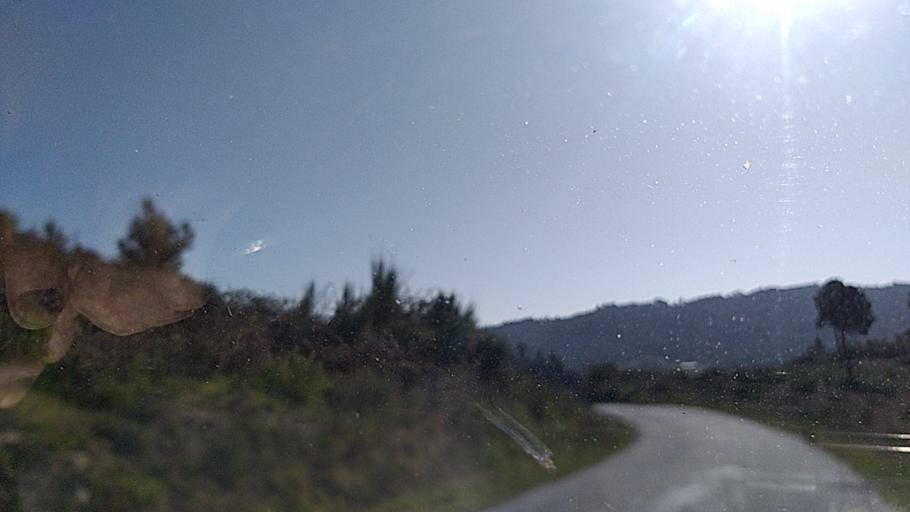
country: PT
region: Guarda
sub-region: Celorico da Beira
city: Celorico da Beira
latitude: 40.6857
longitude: -7.4156
